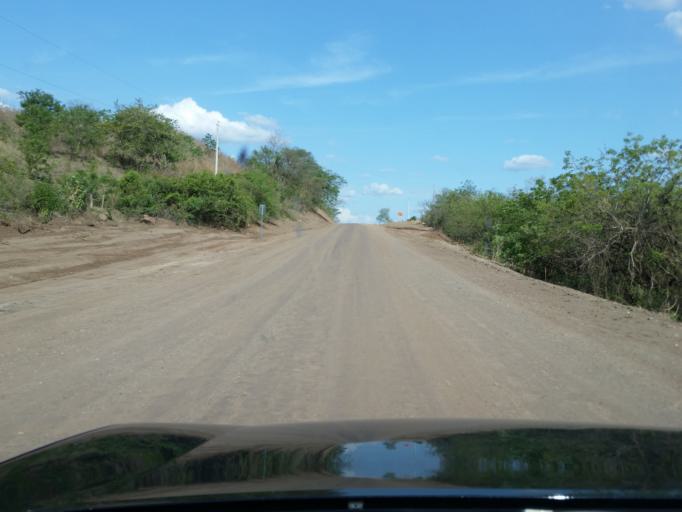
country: NI
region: Leon
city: Nagarote
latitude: 12.1288
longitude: -86.6388
